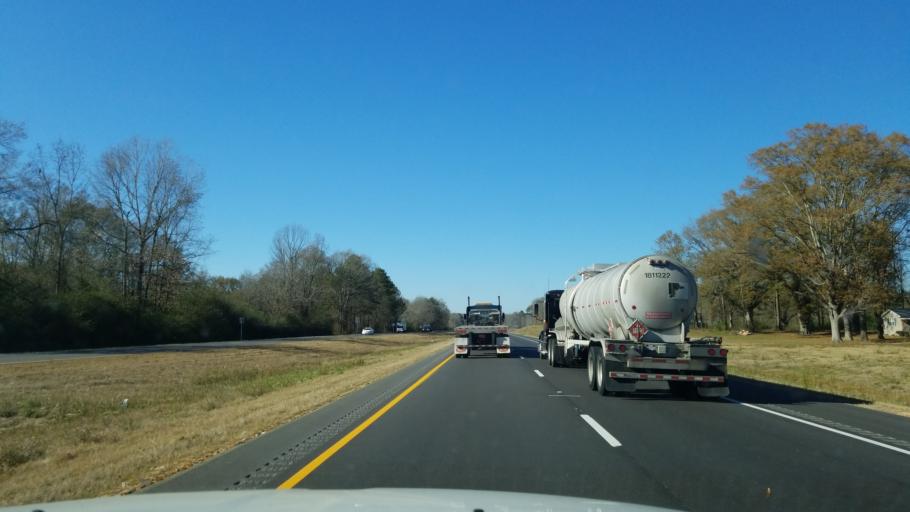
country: US
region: Alabama
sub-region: Pickens County
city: Gordo
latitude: 33.3412
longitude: -87.9404
